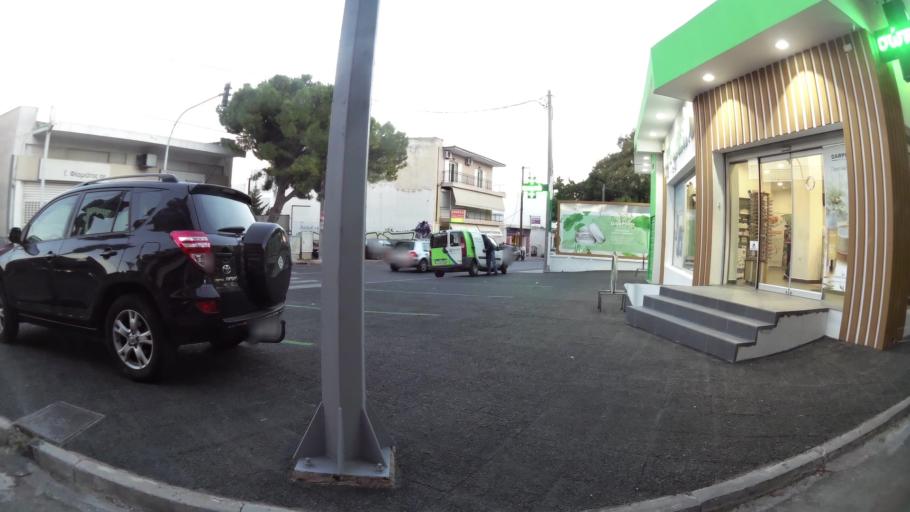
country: GR
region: Attica
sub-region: Nomarchia Anatolikis Attikis
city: Paiania
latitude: 37.9587
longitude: 23.8566
